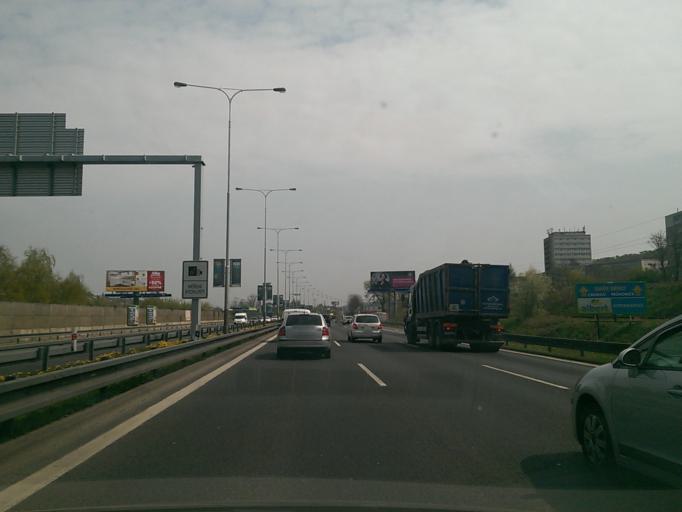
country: CZ
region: Praha
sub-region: Praha 4
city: Hodkovicky
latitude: 50.0322
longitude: 14.4207
